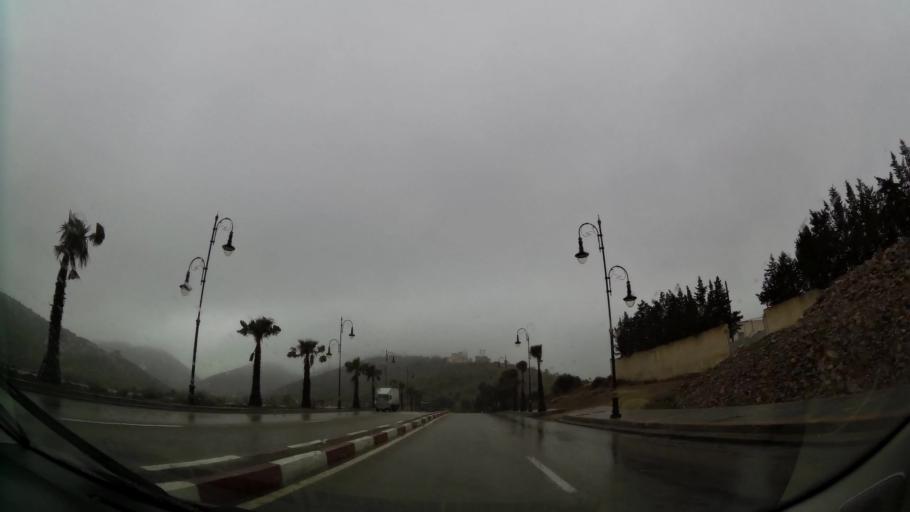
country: MA
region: Taza-Al Hoceima-Taounate
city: Al Hoceima
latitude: 35.2149
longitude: -3.9174
